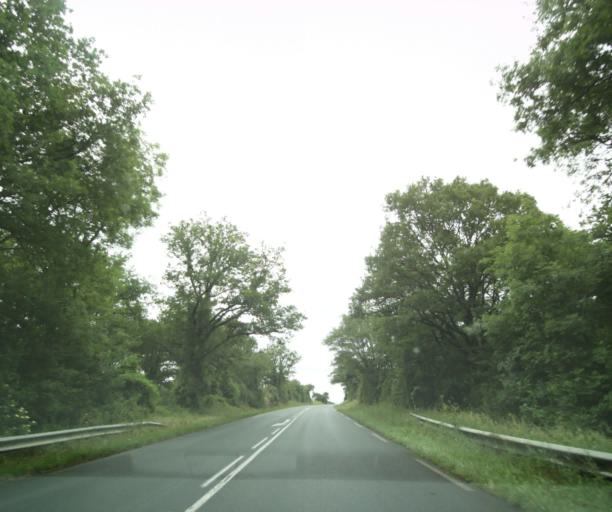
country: FR
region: Poitou-Charentes
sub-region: Departement des Deux-Sevres
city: Viennay
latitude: 46.7120
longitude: -0.2395
